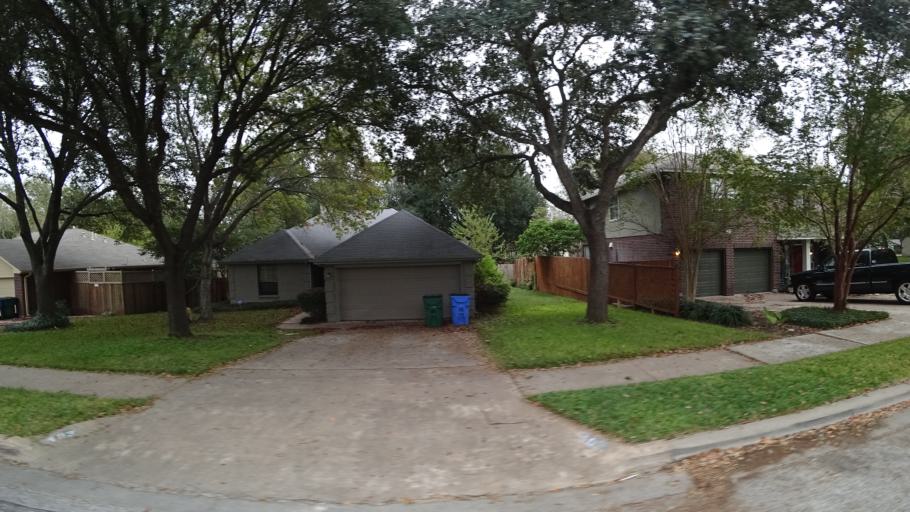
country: US
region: Texas
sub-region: Travis County
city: Pflugerville
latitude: 30.4460
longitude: -97.6258
